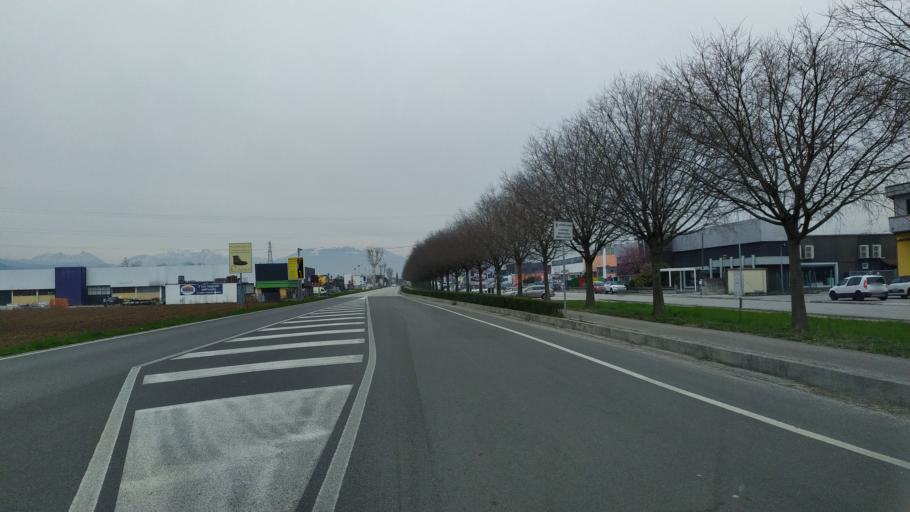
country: IT
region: Veneto
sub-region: Provincia di Vicenza
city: Crispi Cavour
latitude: 45.5867
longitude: 11.5024
